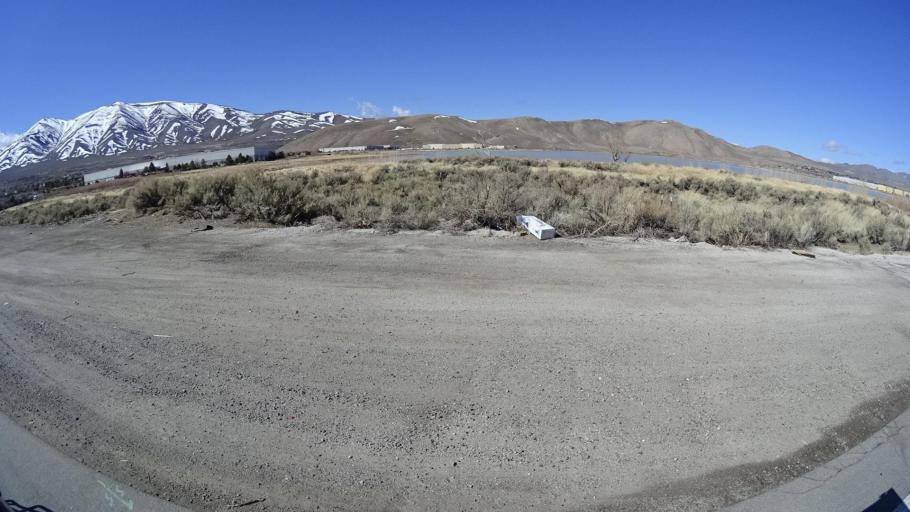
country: US
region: Nevada
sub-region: Washoe County
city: Lemmon Valley
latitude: 39.6392
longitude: -119.8972
